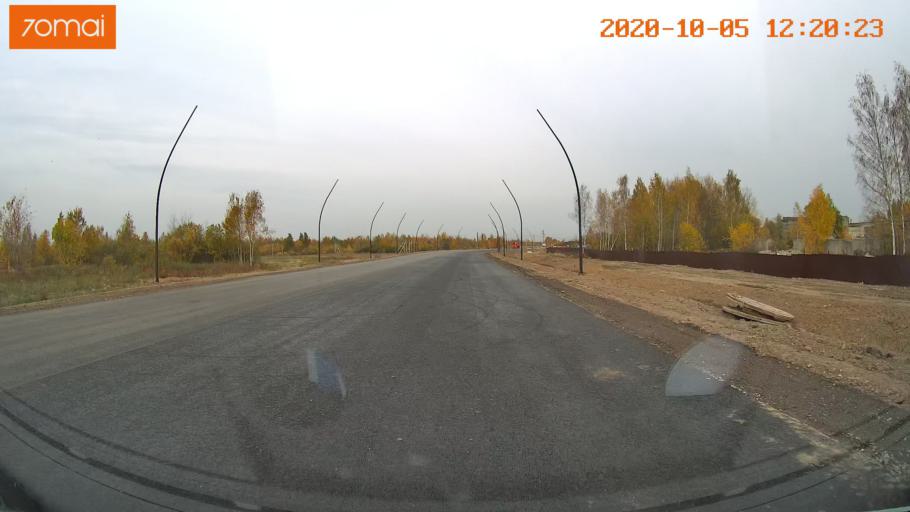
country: RU
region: Ivanovo
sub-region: Gorod Ivanovo
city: Ivanovo
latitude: 56.9628
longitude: 40.9307
